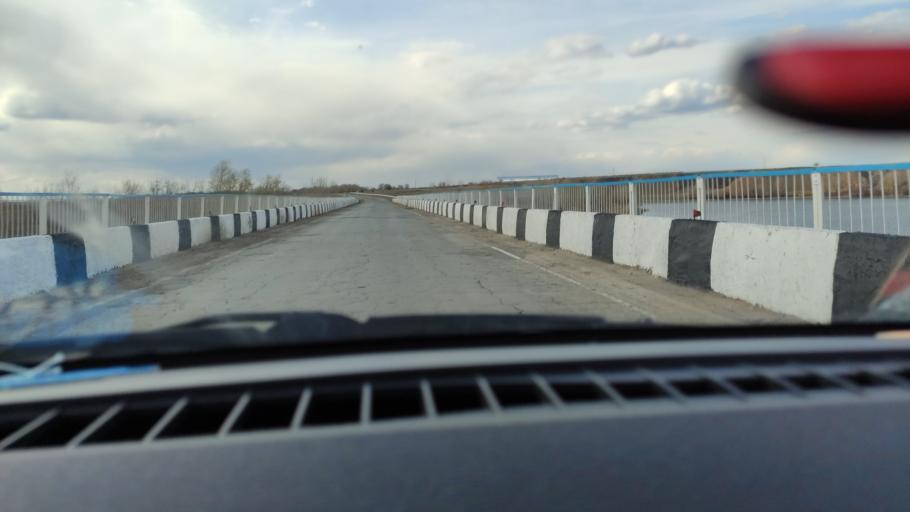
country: RU
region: Saratov
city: Rovnoye
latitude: 51.0337
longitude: 46.0835
